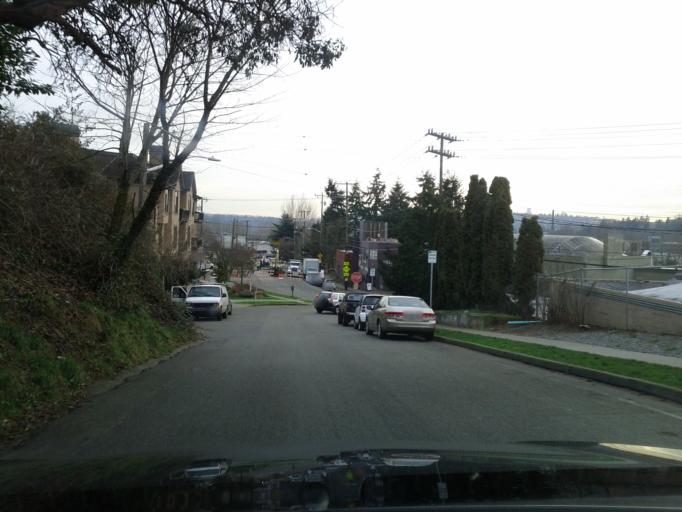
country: US
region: Washington
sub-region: King County
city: Seattle
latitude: 47.6658
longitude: -122.2957
